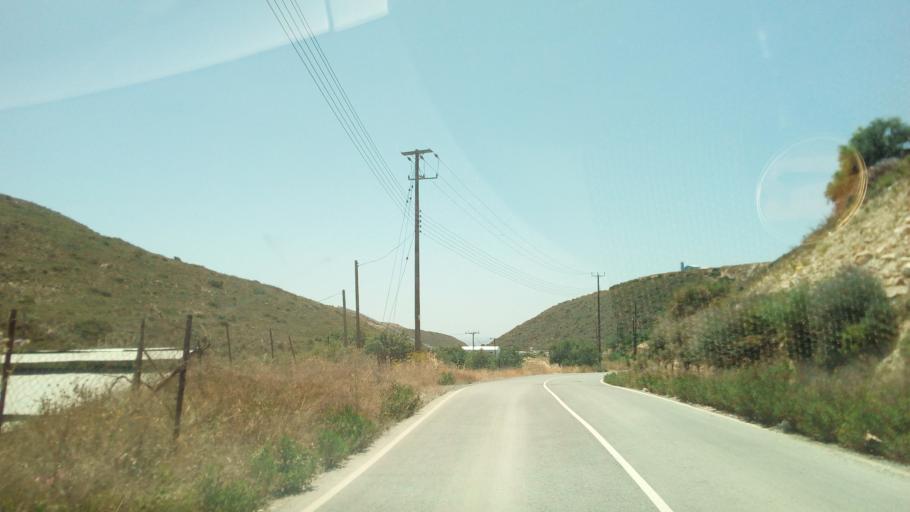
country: CY
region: Limassol
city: Ypsonas
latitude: 34.7447
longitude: 32.9440
